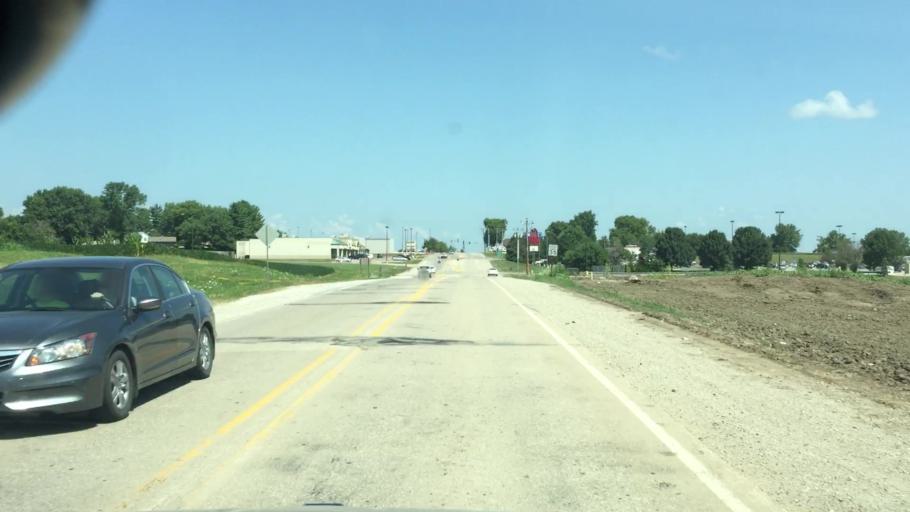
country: US
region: Iowa
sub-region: Jasper County
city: Newton
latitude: 41.6944
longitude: -93.0144
